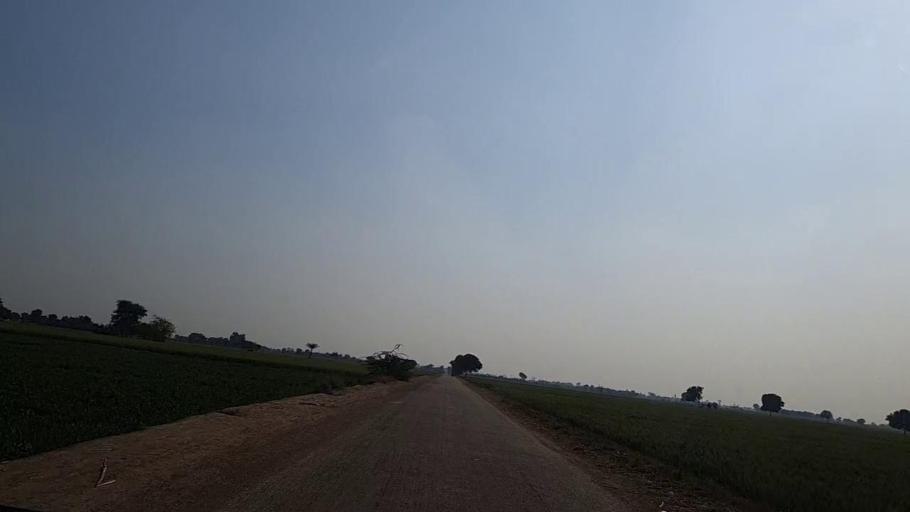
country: PK
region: Sindh
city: Sakrand
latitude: 26.0901
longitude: 68.2903
